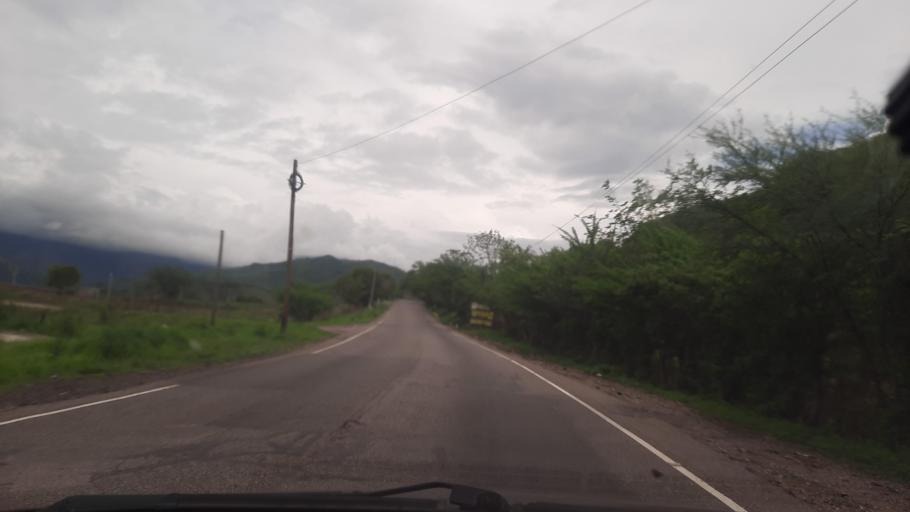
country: GT
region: Zacapa
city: San Jorge
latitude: 14.8932
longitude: -89.5217
